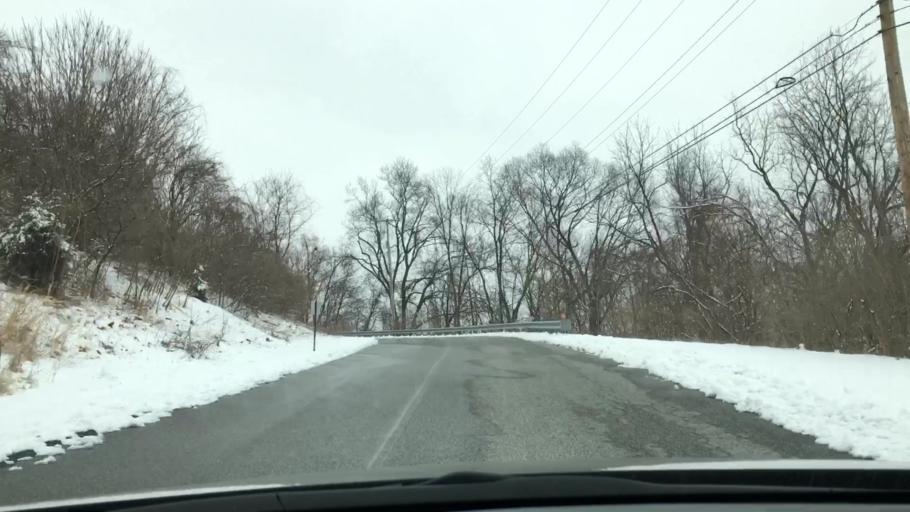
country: US
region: Pennsylvania
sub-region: York County
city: Emigsville
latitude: 40.0225
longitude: -76.7262
